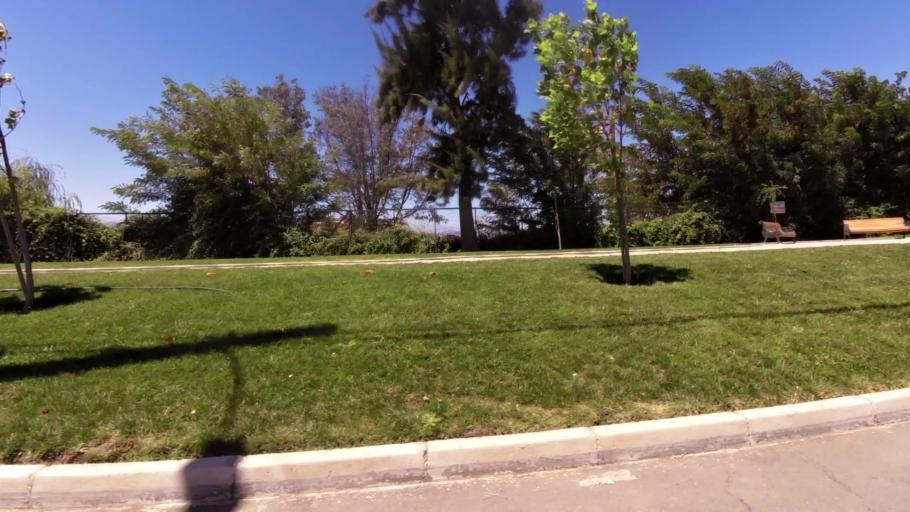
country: CL
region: O'Higgins
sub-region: Provincia de Cachapoal
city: Rancagua
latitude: -34.1524
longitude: -70.7609
